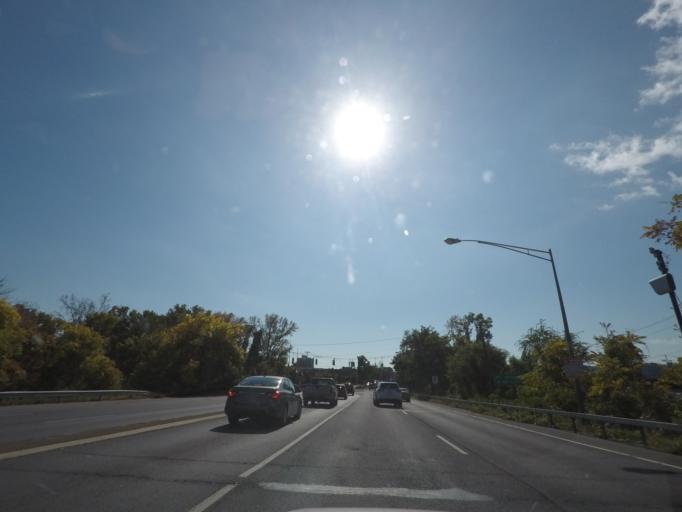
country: US
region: New York
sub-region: Albany County
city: West Albany
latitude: 42.6812
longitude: -73.7856
